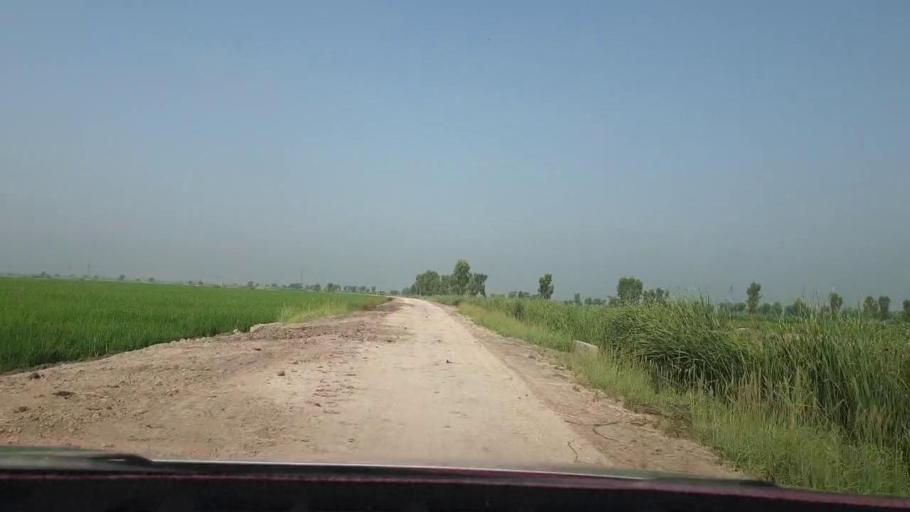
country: PK
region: Sindh
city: Nasirabad
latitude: 27.4311
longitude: 67.9542
